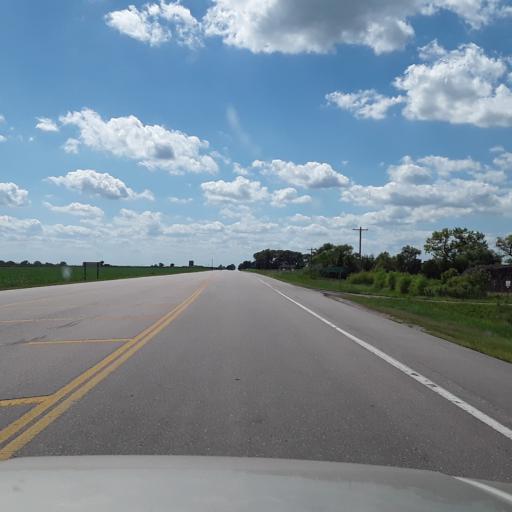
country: US
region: Nebraska
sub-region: Merrick County
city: Central City
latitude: 41.1911
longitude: -97.9834
